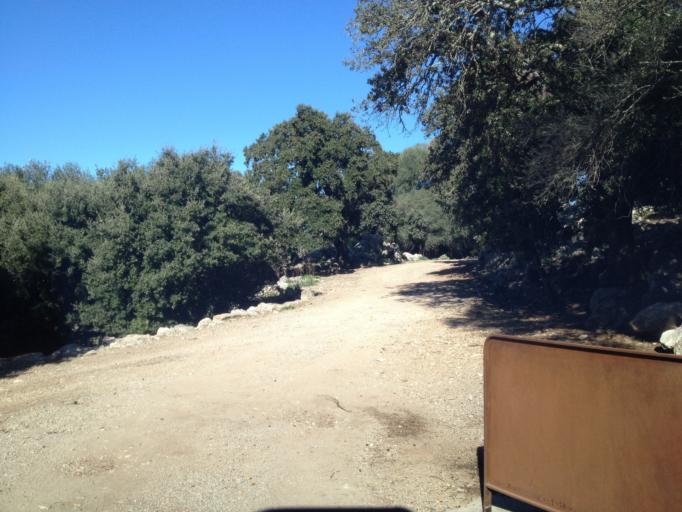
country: ES
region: Balearic Islands
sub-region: Illes Balears
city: Escorca
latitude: 39.8690
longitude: 2.9229
